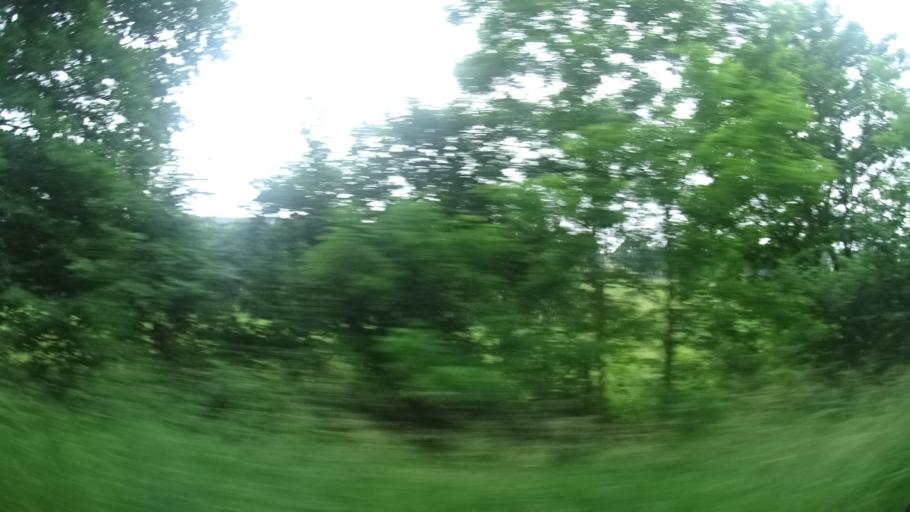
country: DE
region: Hesse
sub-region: Regierungsbezirk Darmstadt
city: Bad Soden-Salmunster
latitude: 50.2695
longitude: 9.3903
